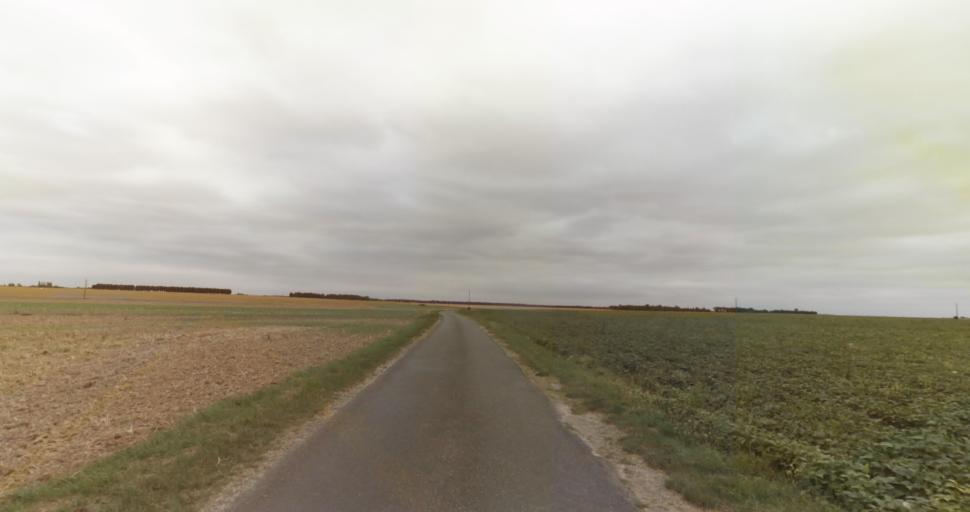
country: FR
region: Haute-Normandie
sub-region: Departement de l'Eure
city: La Couture-Boussey
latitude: 48.9317
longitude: 1.3967
